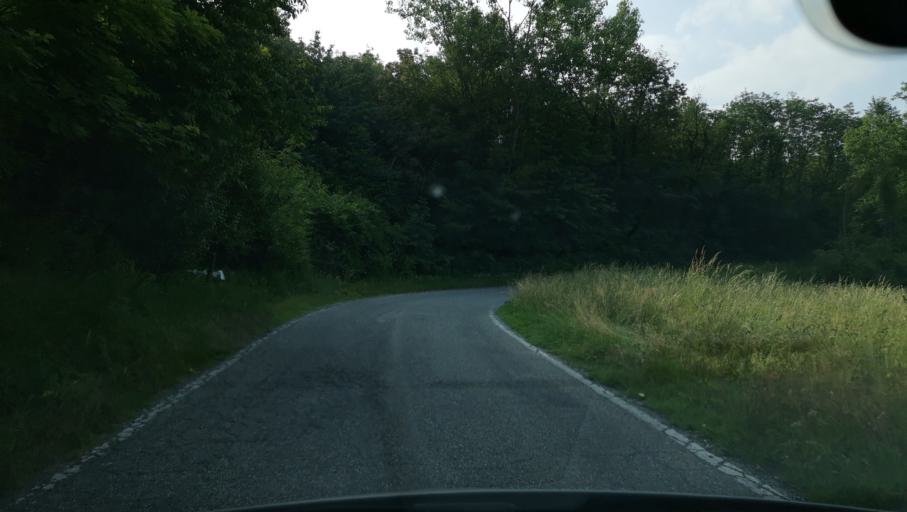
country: IT
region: Piedmont
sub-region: Provincia di Alessandria
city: Villadeati
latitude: 45.0815
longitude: 8.1819
